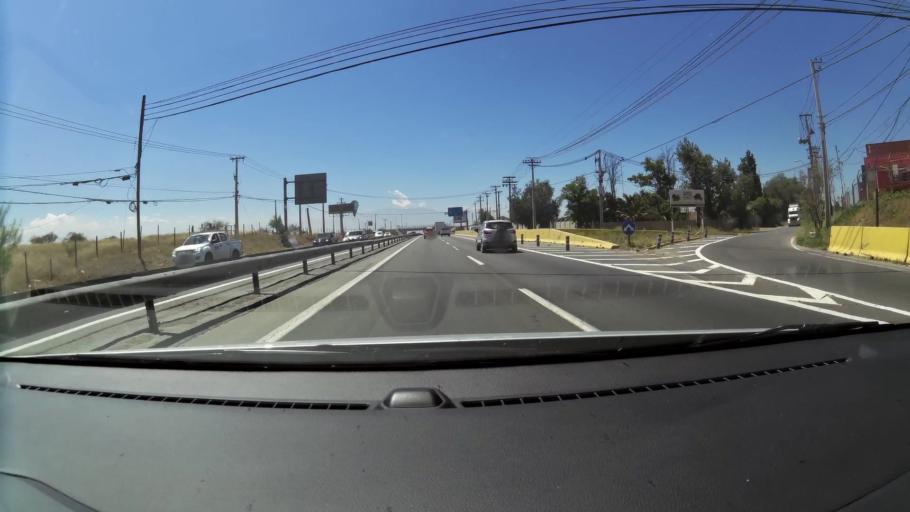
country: CL
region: Santiago Metropolitan
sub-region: Provincia de Santiago
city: Lo Prado
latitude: -33.4387
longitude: -70.8167
